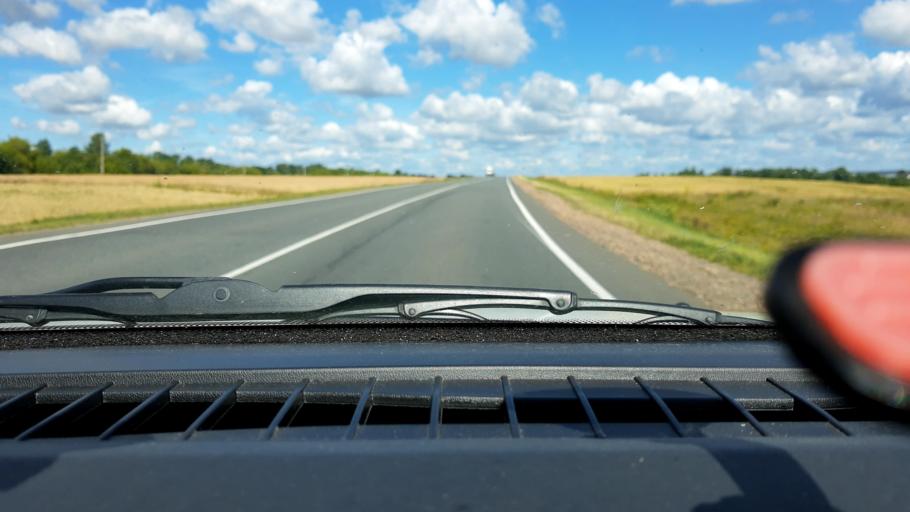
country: RU
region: Nizjnij Novgorod
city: Shatki
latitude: 55.2527
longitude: 43.9854
